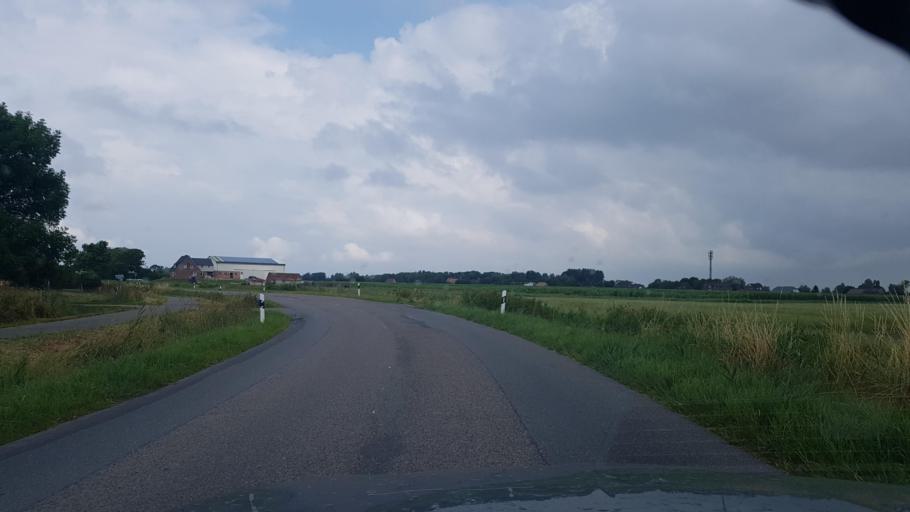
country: DE
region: Schleswig-Holstein
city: Elisabeth-Sophien-Koog
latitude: 54.4931
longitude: 8.8496
